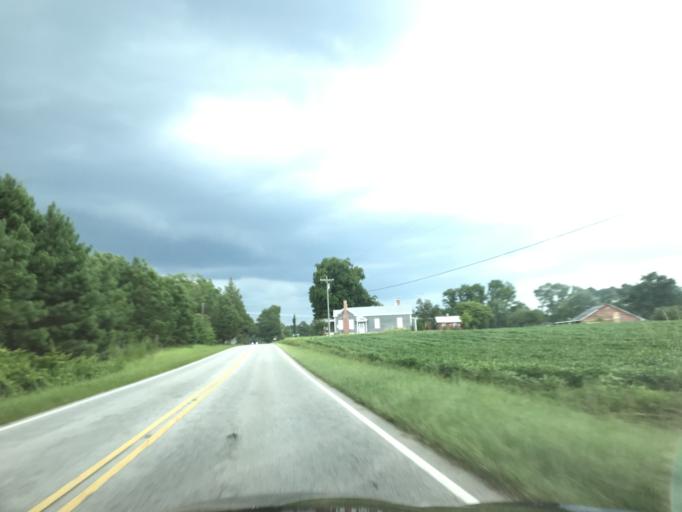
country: US
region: North Carolina
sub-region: Johnston County
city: Four Oaks
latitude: 35.5113
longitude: -78.5111
